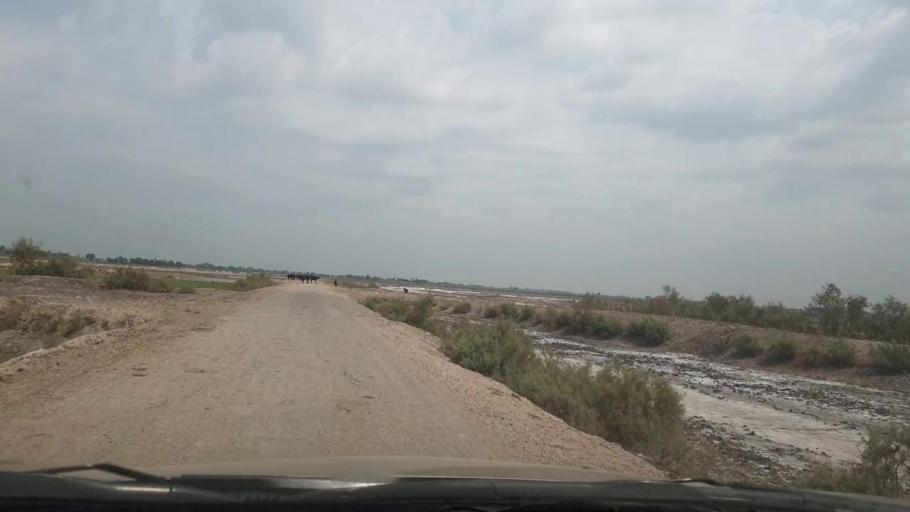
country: PK
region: Sindh
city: Ratodero
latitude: 27.7055
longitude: 68.2289
